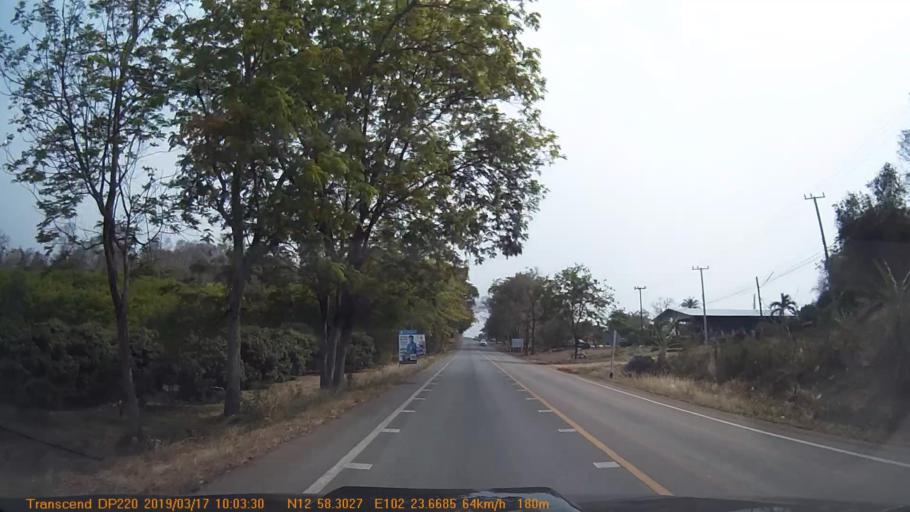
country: TH
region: Chanthaburi
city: Pong Nam Ron
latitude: 12.9731
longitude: 102.3956
